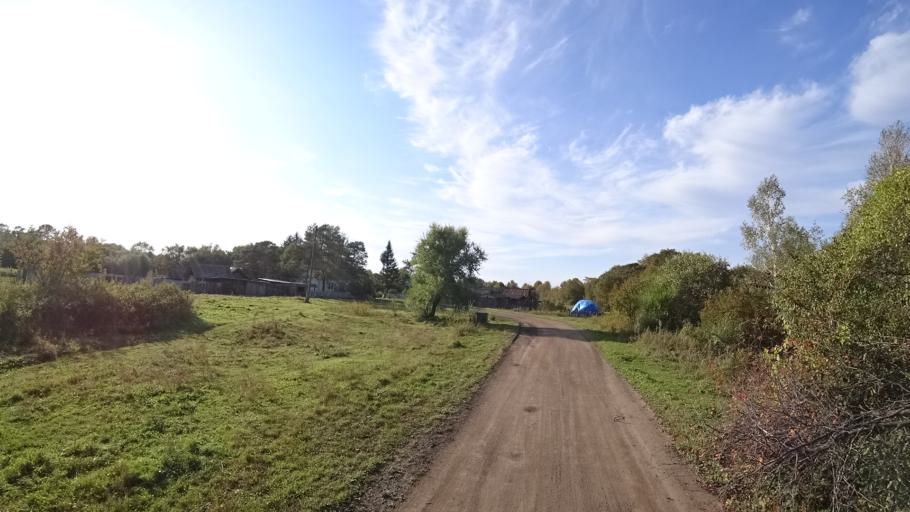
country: RU
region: Amur
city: Arkhara
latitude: 49.3506
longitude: 130.1141
